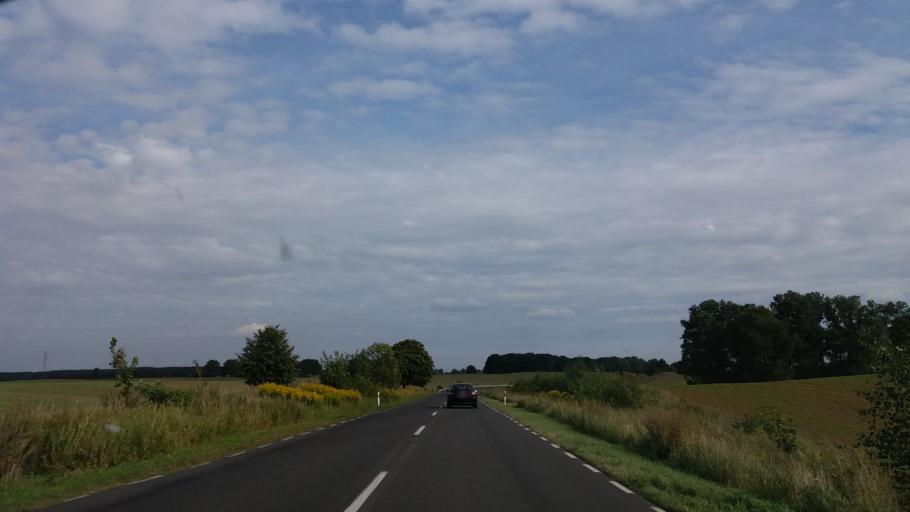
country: PL
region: West Pomeranian Voivodeship
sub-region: Powiat choszczenski
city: Choszczno
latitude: 53.1953
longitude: 15.3794
